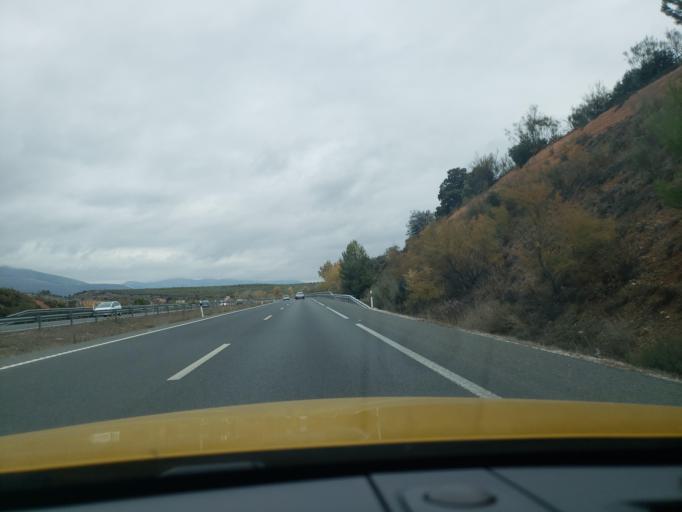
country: ES
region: Andalusia
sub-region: Provincia de Granada
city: Calicasas
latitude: 37.2904
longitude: -3.6574
